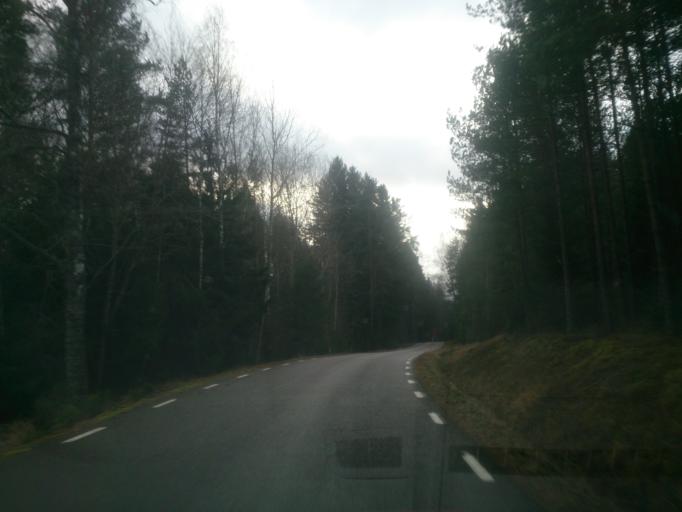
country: SE
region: OEstergoetland
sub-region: Norrkopings Kommun
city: Krokek
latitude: 58.5295
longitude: 16.6094
